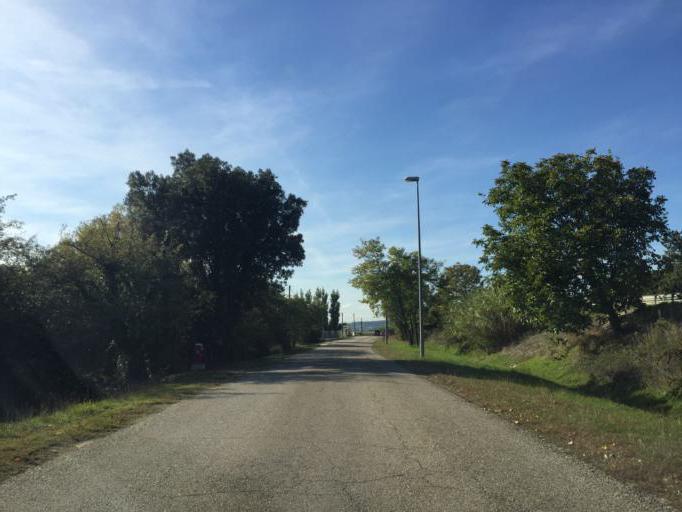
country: FR
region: Rhone-Alpes
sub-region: Departement de la Drome
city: Pierrelatte
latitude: 44.3594
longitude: 4.7048
